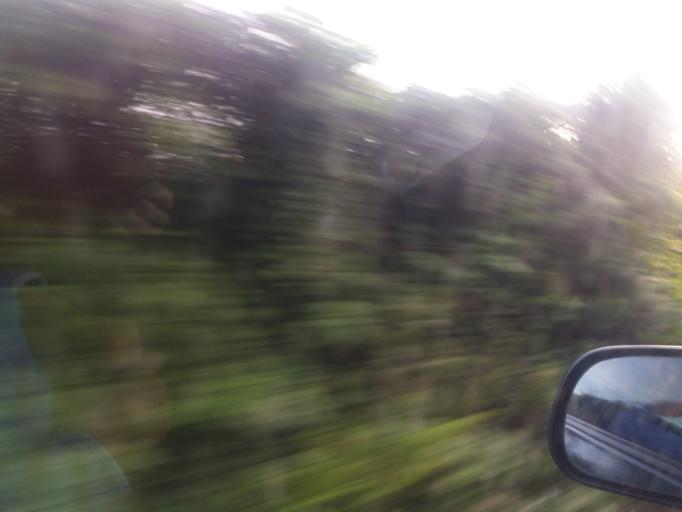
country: IE
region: Leinster
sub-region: Fingal County
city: Swords
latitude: 53.4905
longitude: -6.1992
